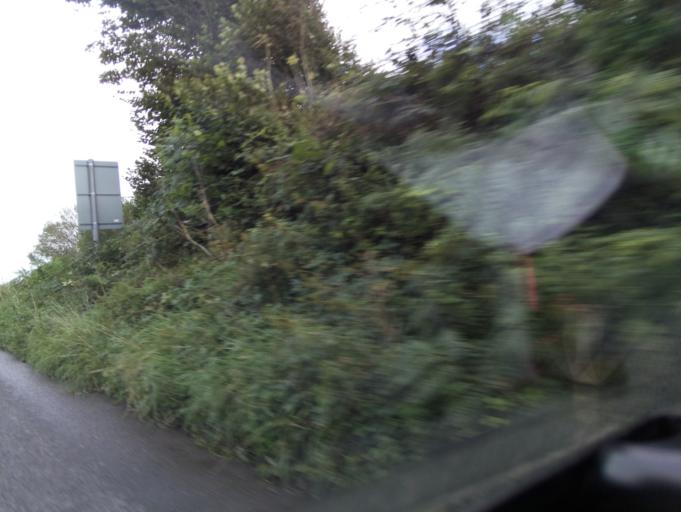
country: GB
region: England
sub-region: Devon
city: Modbury
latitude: 50.3403
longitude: -3.8679
